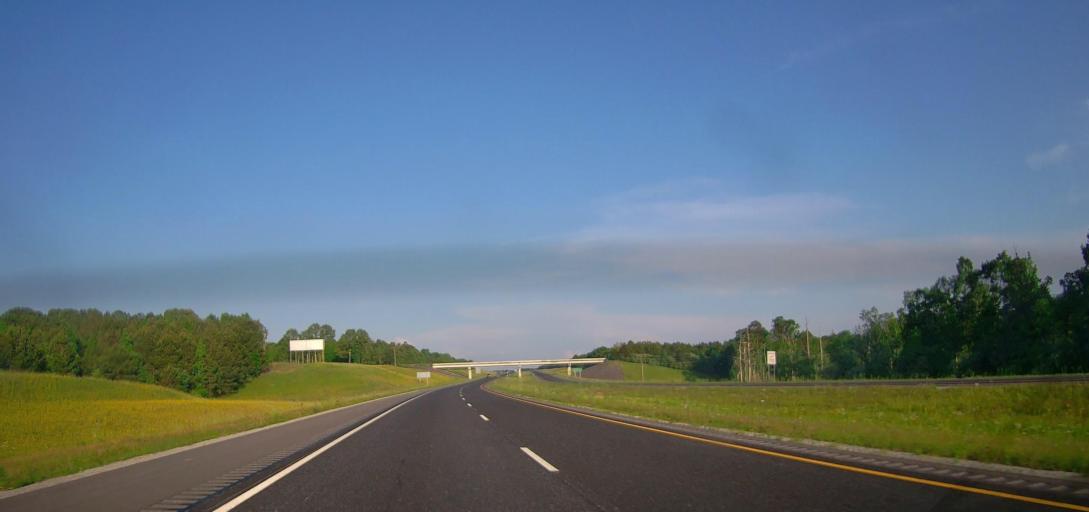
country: US
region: Alabama
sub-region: Marion County
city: Winfield
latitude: 33.9868
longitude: -87.7658
